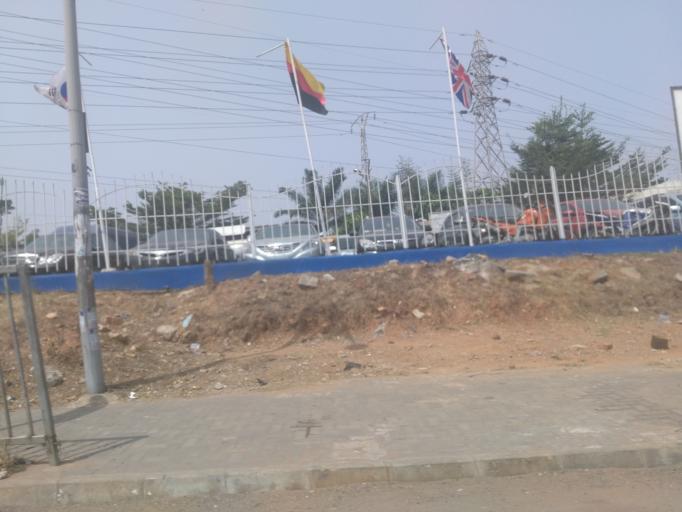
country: GH
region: Greater Accra
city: Dome
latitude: 5.6179
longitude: -0.1931
